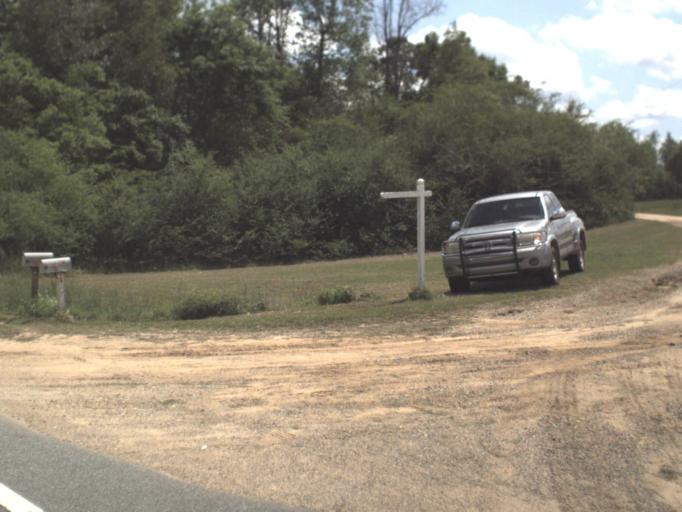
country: US
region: Florida
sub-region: Escambia County
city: Molino
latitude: 30.7816
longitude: -87.4030
